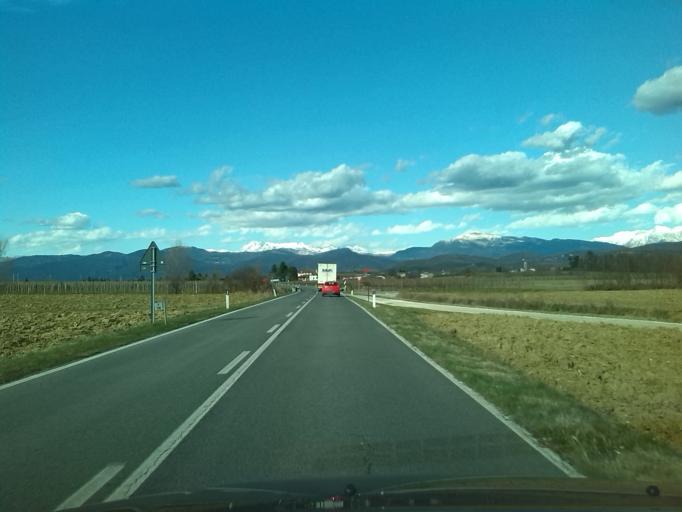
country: IT
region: Friuli Venezia Giulia
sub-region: Provincia di Gorizia
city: Dolegna del Collio
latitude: 46.0292
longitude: 13.4418
